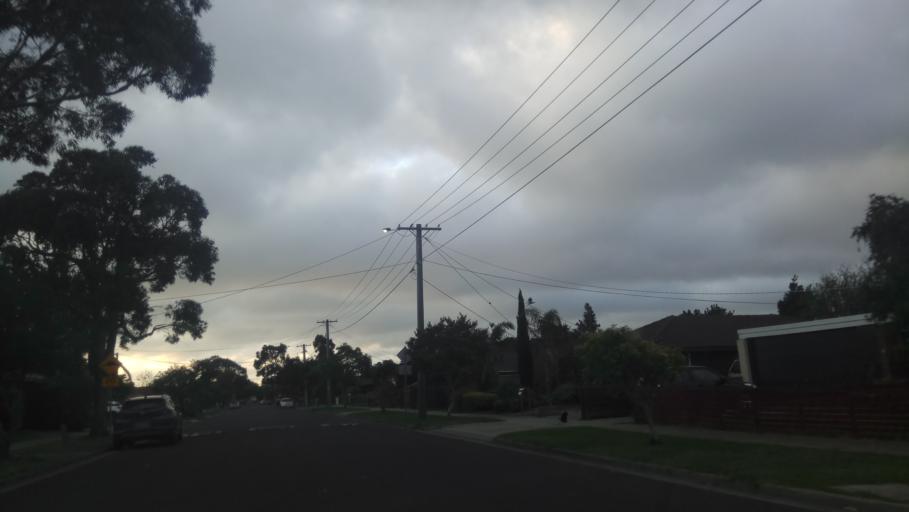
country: AU
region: Victoria
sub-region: Hobsons Bay
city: Altona Meadows
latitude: -37.8913
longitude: 144.7806
